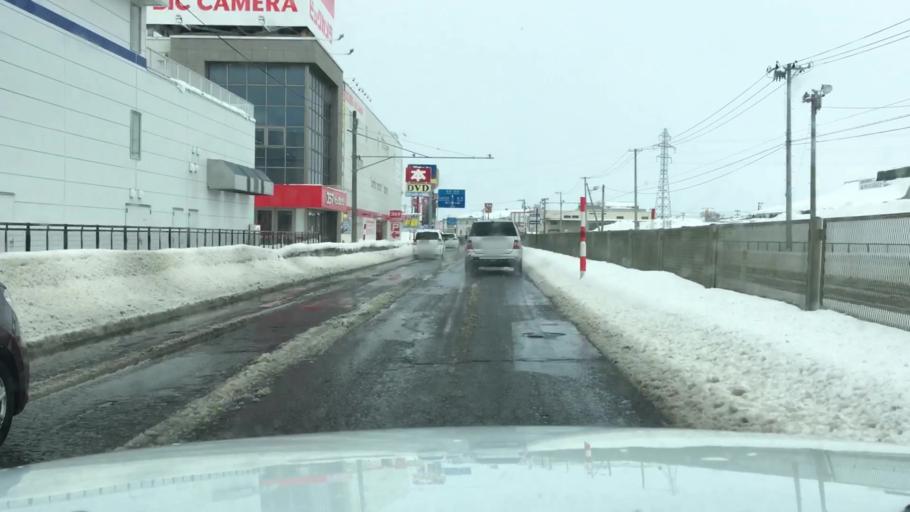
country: JP
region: Aomori
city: Hirosaki
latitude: 40.6071
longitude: 140.4989
